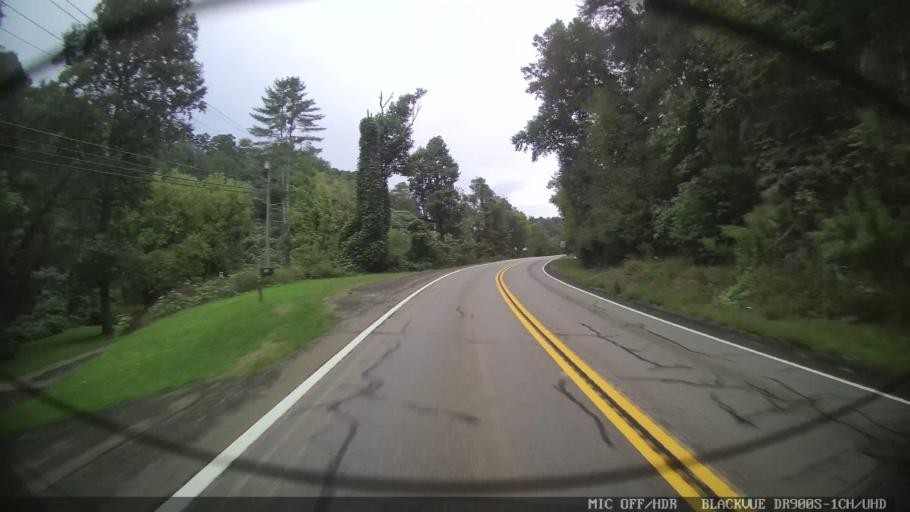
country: US
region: Georgia
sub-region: Gilmer County
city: Ellijay
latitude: 34.7054
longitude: -84.4888
